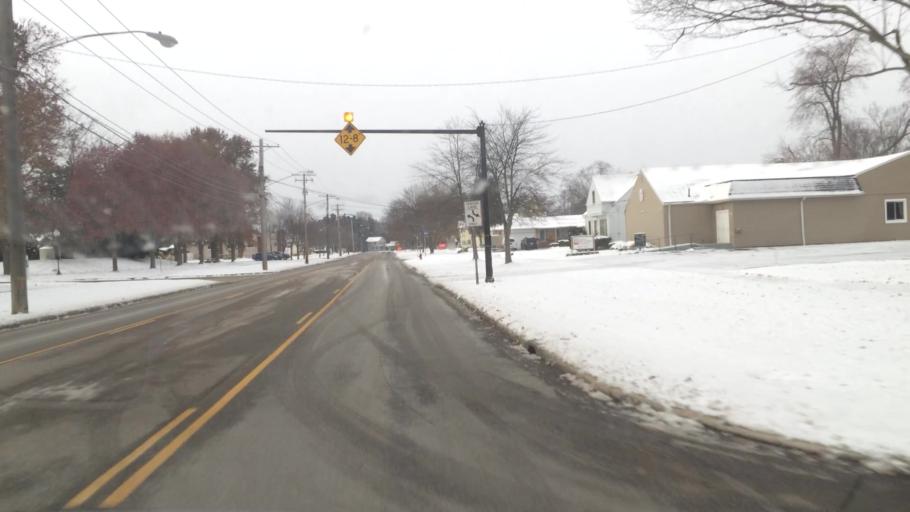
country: US
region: Ohio
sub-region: Cuyahoga County
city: Berea
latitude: 41.3840
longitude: -81.8564
